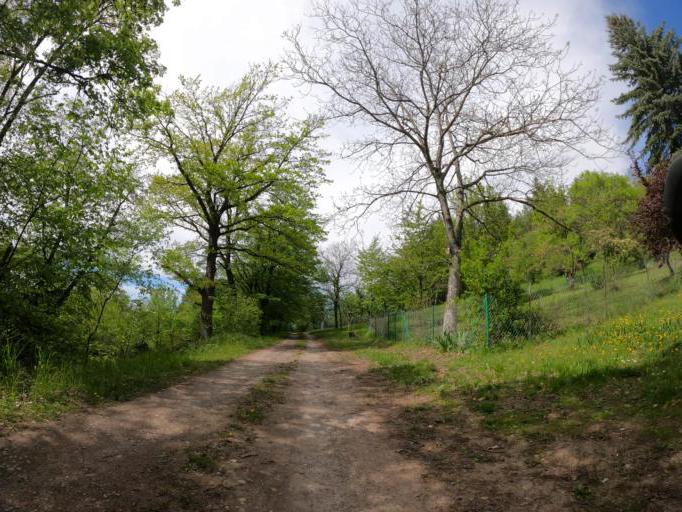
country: DE
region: Baden-Wuerttemberg
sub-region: Karlsruhe Region
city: Konigsbach-Stein
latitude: 48.9302
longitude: 8.6140
